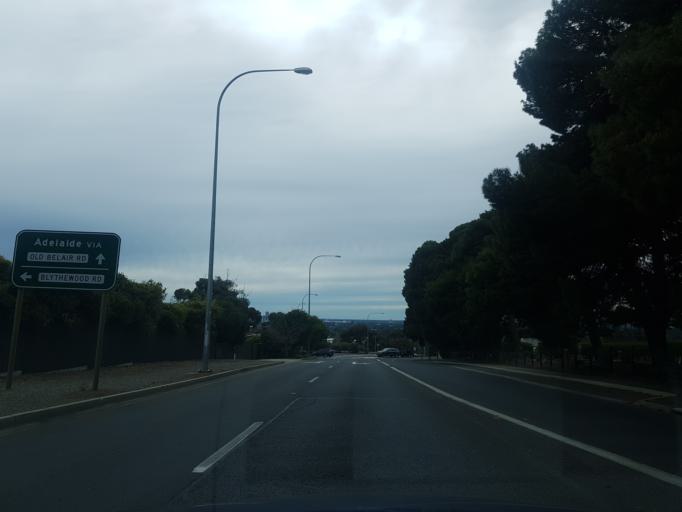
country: AU
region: South Australia
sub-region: Mitcham
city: Mitcham
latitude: -34.9845
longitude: 138.6190
